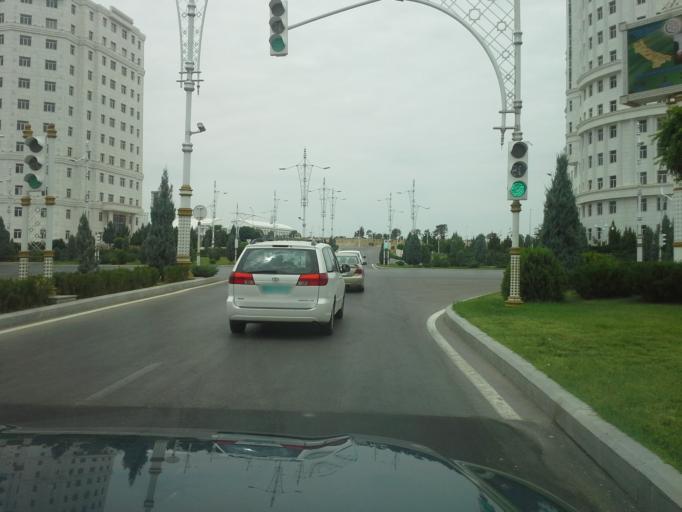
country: TM
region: Ahal
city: Ashgabat
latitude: 37.9210
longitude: 58.3598
